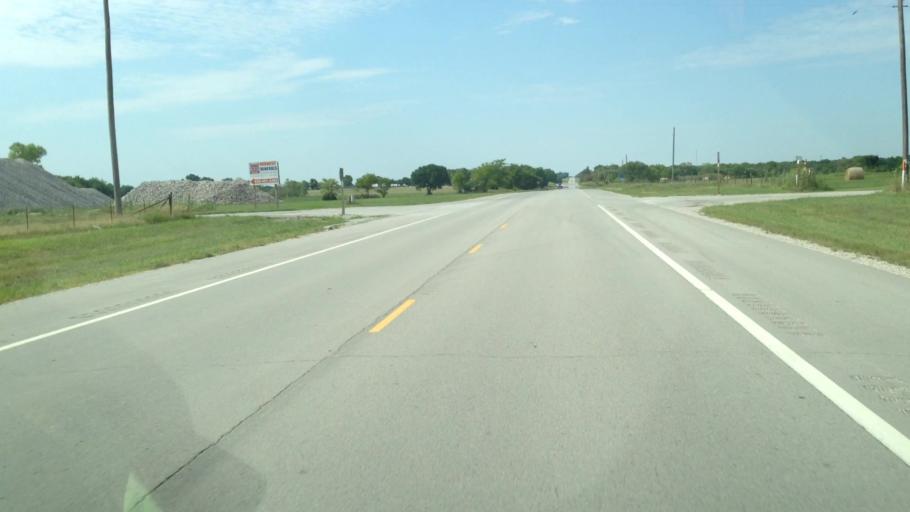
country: US
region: Kansas
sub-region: Labette County
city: Parsons
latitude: 37.2810
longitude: -95.2675
